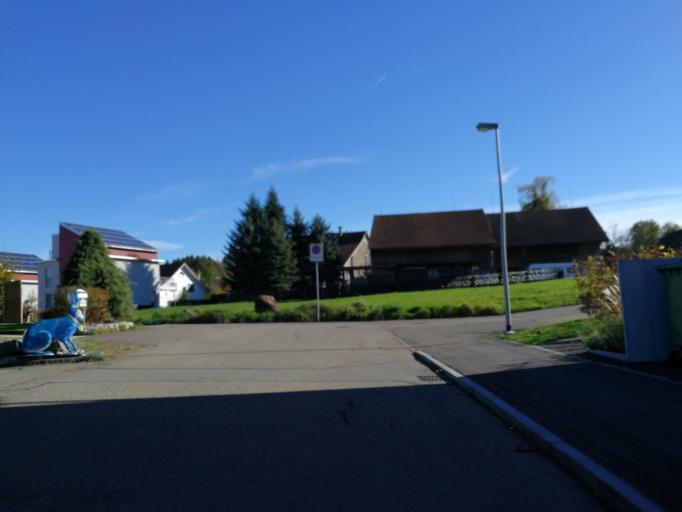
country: CH
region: Zurich
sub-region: Bezirk Meilen
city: Oetwil am See
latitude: 47.2729
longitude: 8.7250
